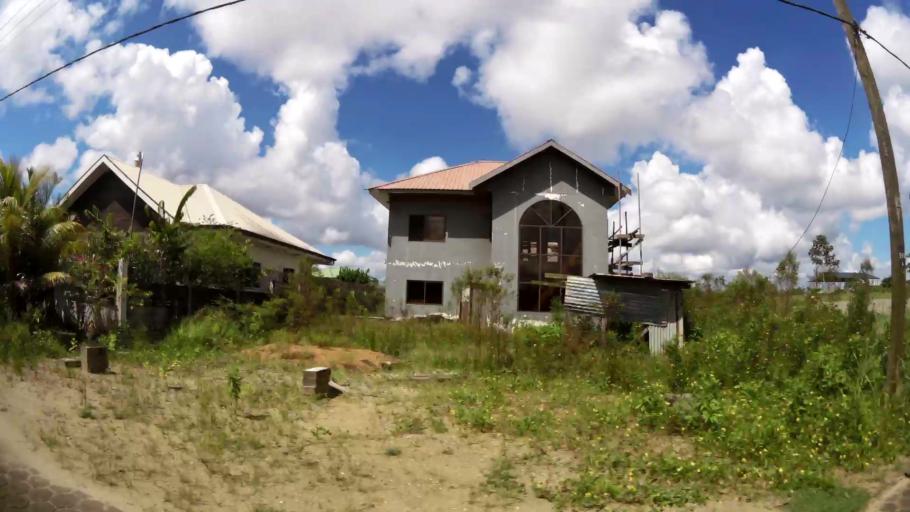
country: SR
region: Paramaribo
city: Paramaribo
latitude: 5.8676
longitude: -55.1331
